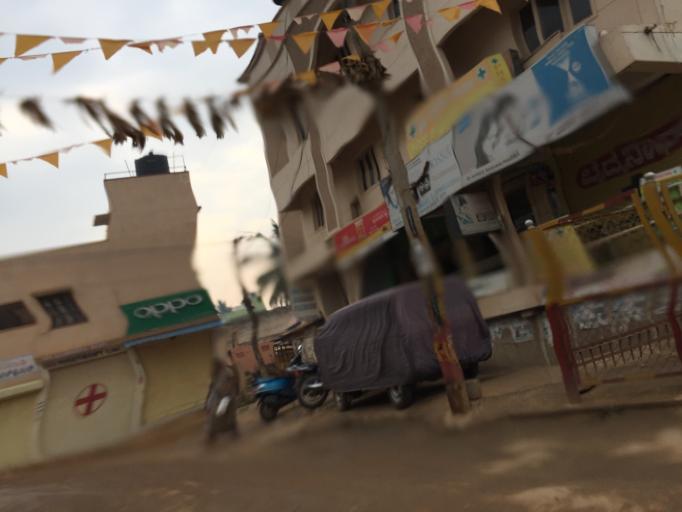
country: IN
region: Karnataka
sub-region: Bangalore Urban
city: Yelahanka
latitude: 13.0561
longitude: 77.6332
